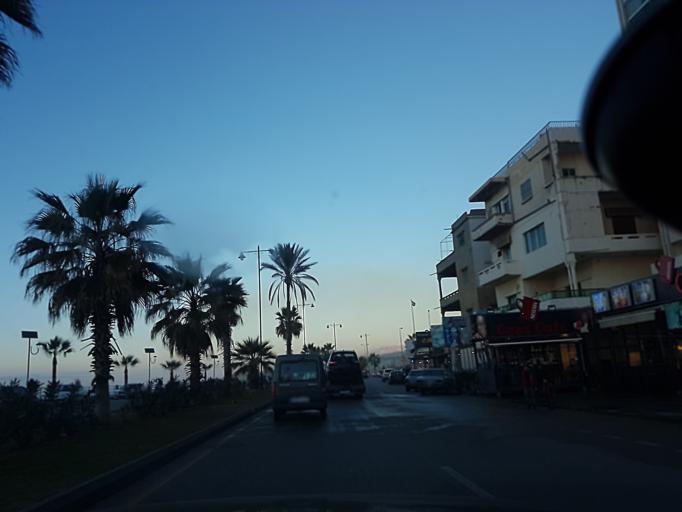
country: LB
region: Liban-Sud
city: Sidon
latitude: 33.5718
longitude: 35.3780
